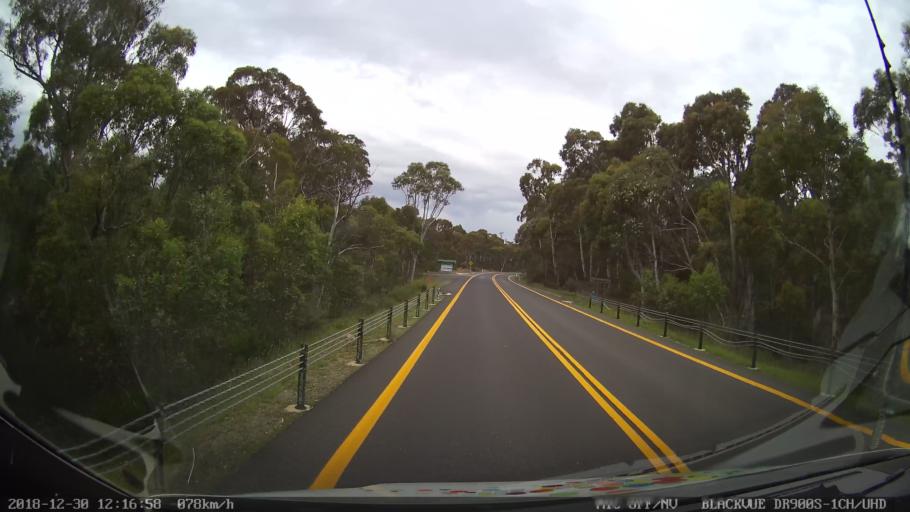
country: AU
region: New South Wales
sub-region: Snowy River
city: Jindabyne
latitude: -36.3503
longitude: 148.5635
